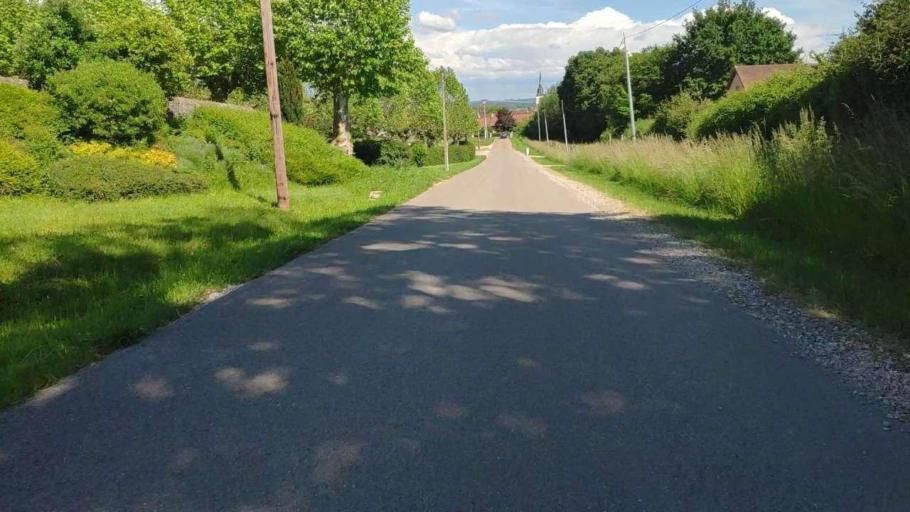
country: FR
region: Franche-Comte
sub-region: Departement du Jura
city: Bletterans
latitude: 46.7662
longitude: 5.4677
